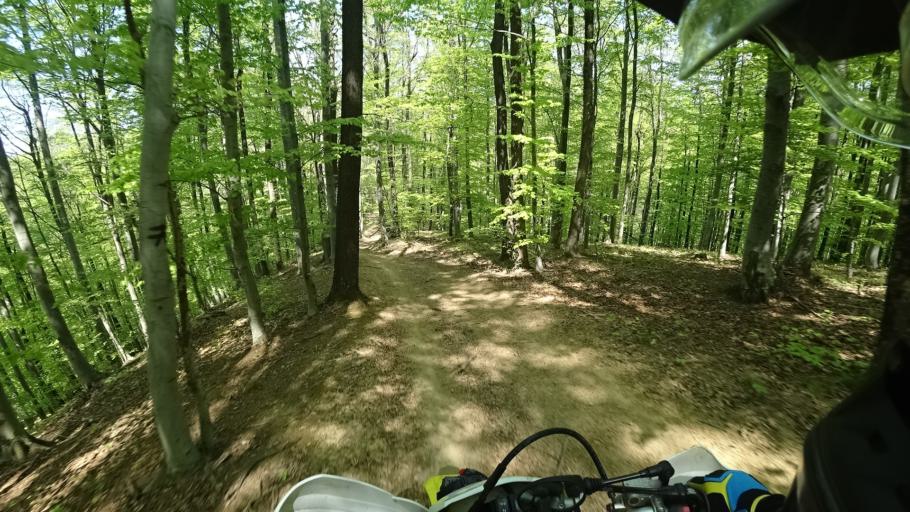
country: HR
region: Zagrebacka
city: Jablanovec
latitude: 45.8637
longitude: 15.9032
